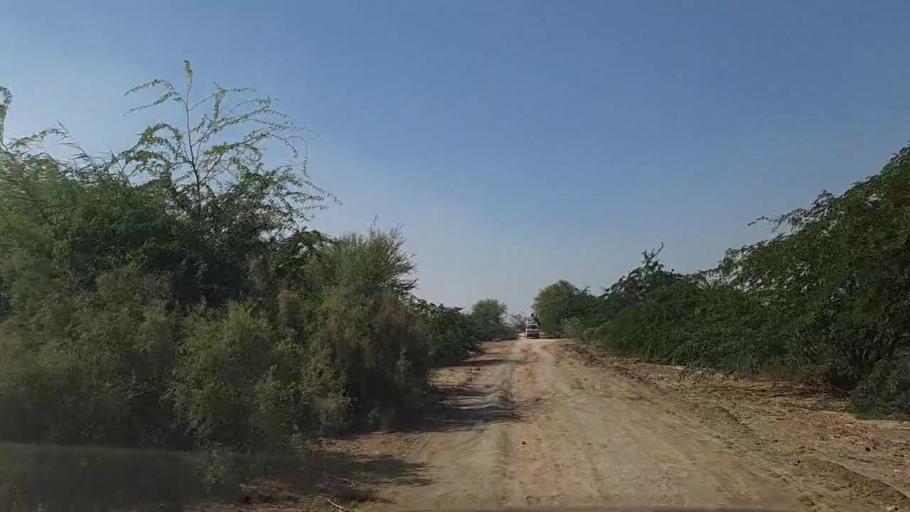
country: PK
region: Sindh
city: Daro Mehar
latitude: 24.8386
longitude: 68.1347
